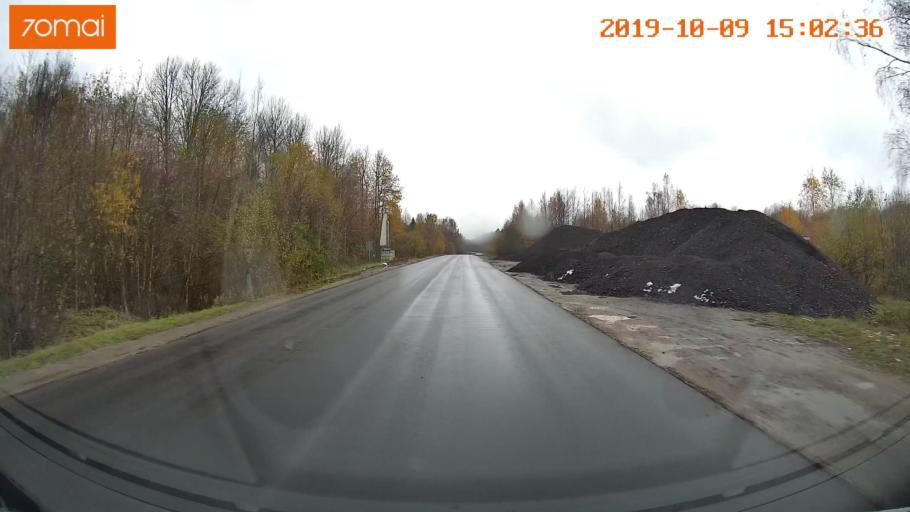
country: RU
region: Kostroma
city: Chistyye Bory
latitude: 58.2827
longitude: 41.6783
